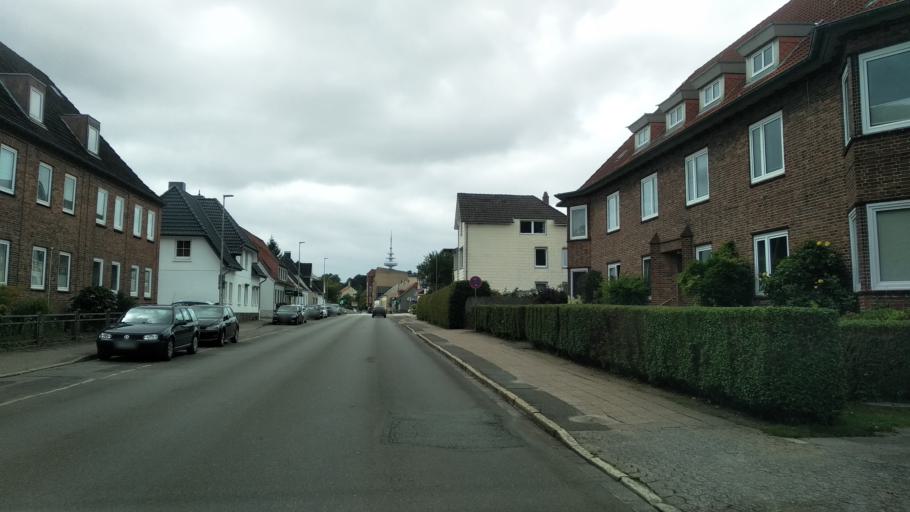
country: DE
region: Schleswig-Holstein
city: Schleswig
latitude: 54.5225
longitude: 9.5478
